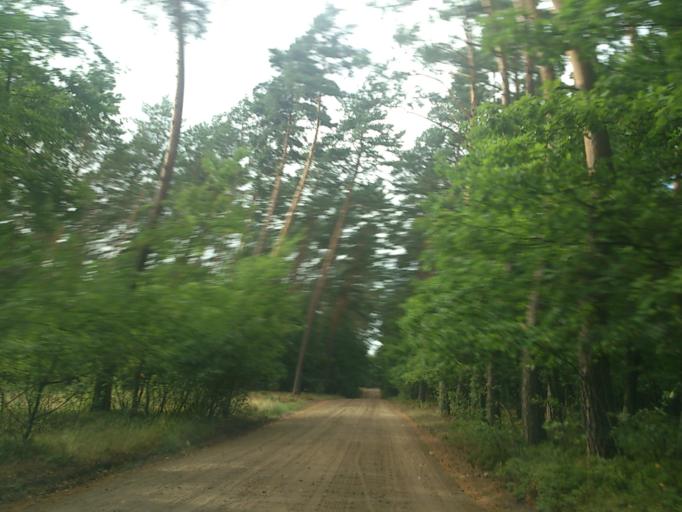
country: PL
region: Greater Poland Voivodeship
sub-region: Powiat poznanski
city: Kobylnica
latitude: 52.5264
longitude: 17.1214
